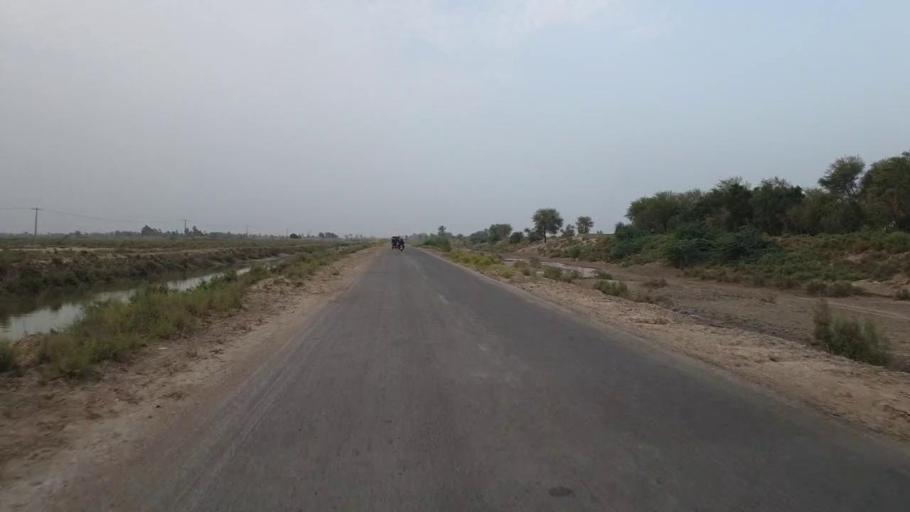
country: PK
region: Sindh
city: Daur
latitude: 26.4453
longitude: 68.2823
